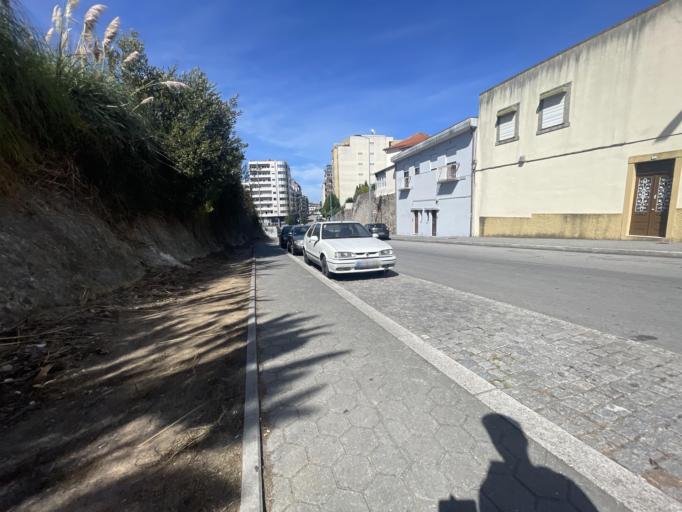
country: PT
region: Porto
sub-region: Vila Nova de Gaia
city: Vila Nova de Gaia
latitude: 41.1351
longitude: -8.6254
